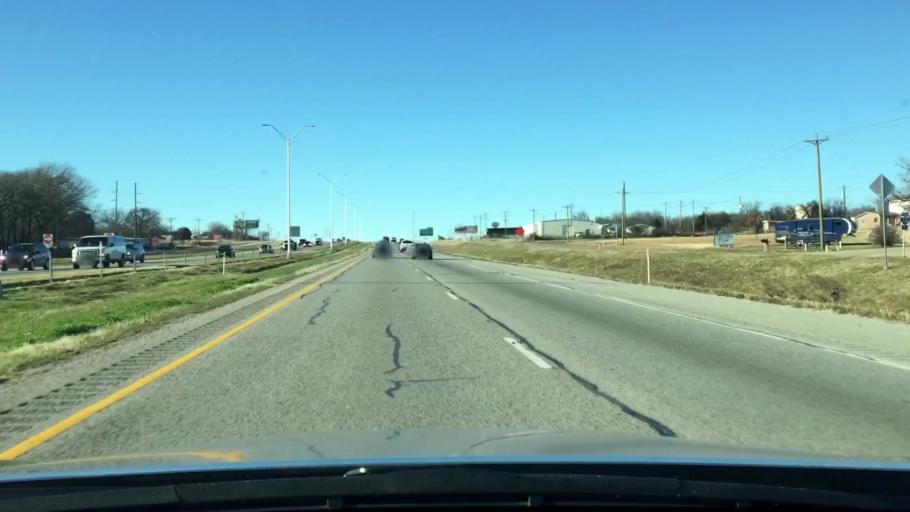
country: US
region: Texas
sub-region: Johnson County
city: Alvarado
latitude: 32.4668
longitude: -97.2676
